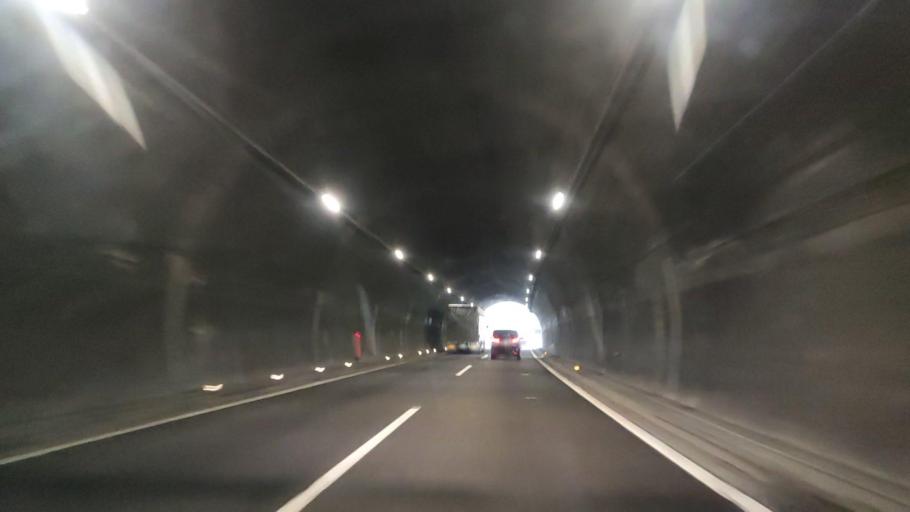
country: JP
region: Hyogo
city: Kariya
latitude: 34.7894
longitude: 134.4033
